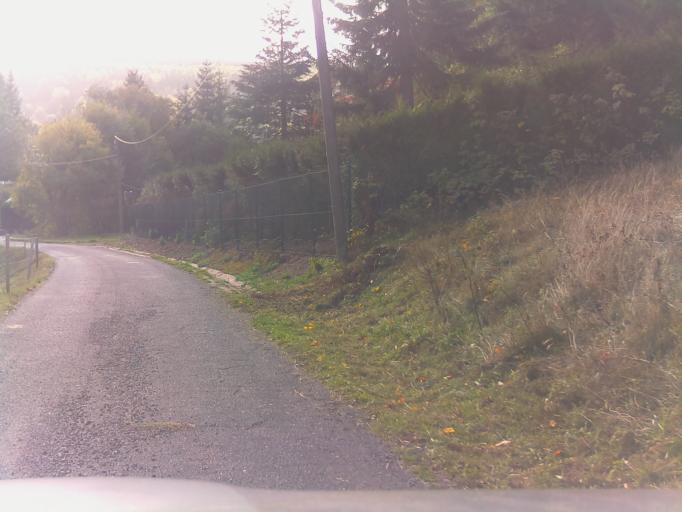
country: DE
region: Thuringia
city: Bermbach
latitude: 50.7175
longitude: 10.6214
